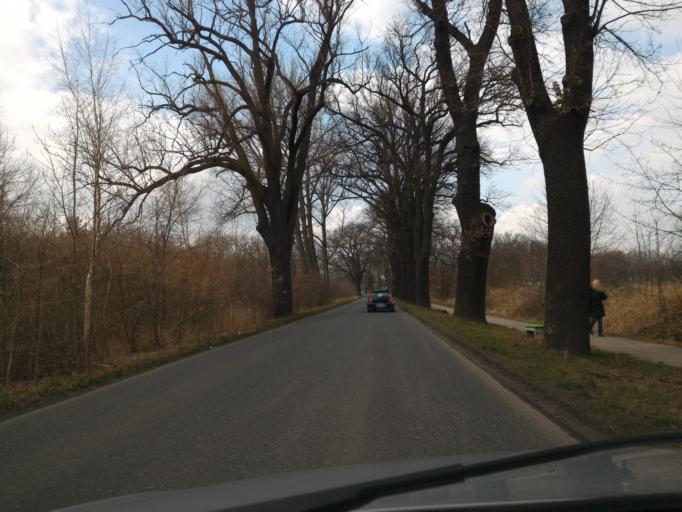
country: DE
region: Saxony
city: Zittau
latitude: 50.8818
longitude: 14.8208
